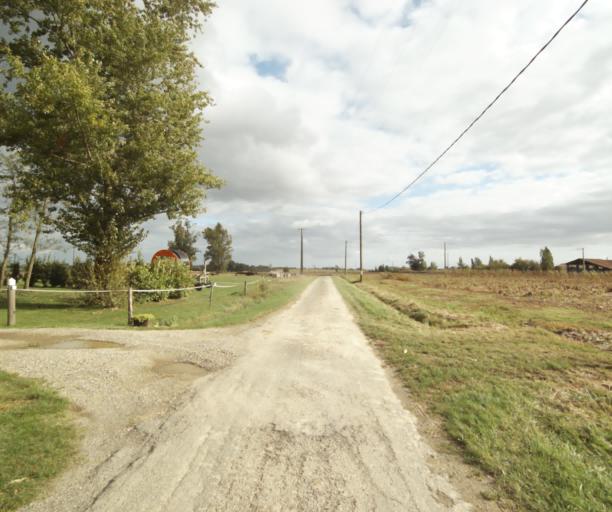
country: FR
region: Midi-Pyrenees
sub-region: Departement du Tarn-et-Garonne
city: Finhan
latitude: 43.8942
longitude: 1.1070
